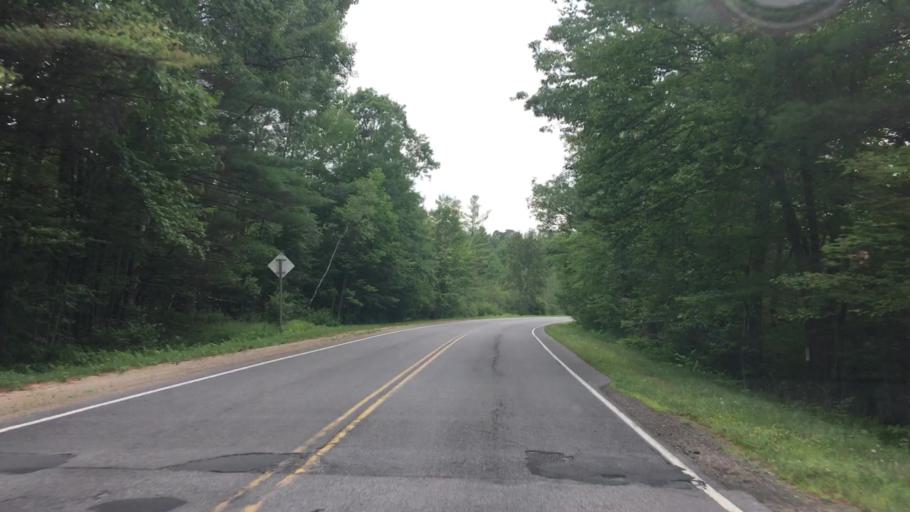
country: US
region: New York
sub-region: Essex County
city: Keeseville
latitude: 44.4789
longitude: -73.5964
